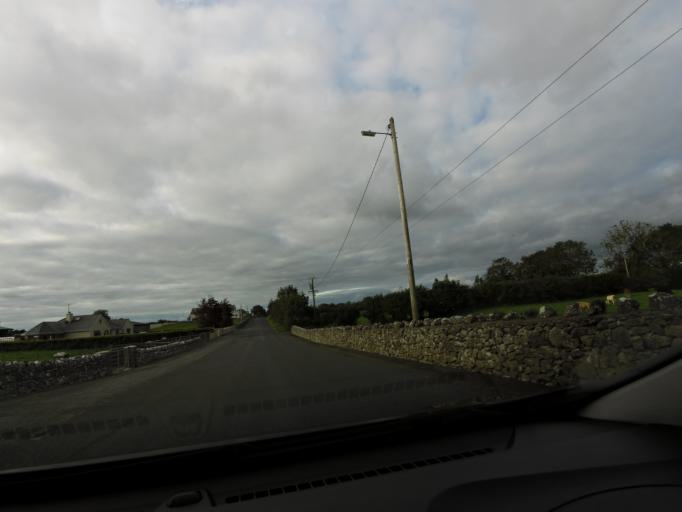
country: IE
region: Connaught
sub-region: County Galway
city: Ballinasloe
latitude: 53.3383
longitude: -8.0933
